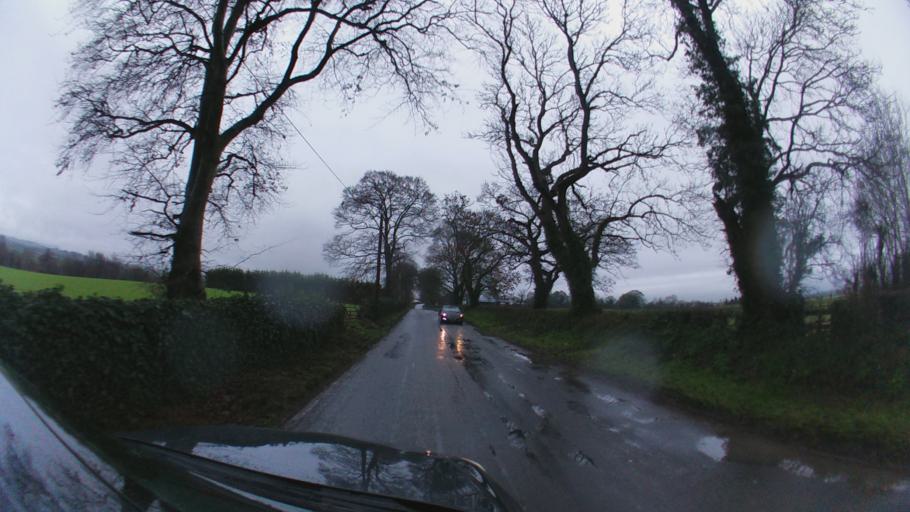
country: IE
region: Leinster
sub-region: County Carlow
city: Bagenalstown
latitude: 52.6622
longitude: -6.9909
